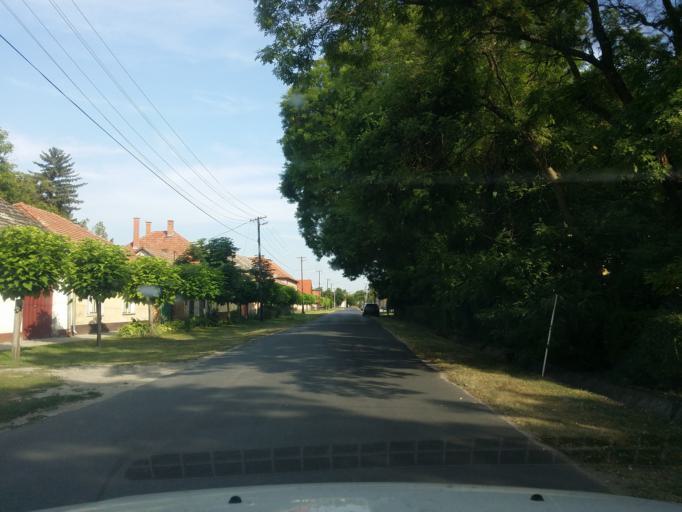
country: HU
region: Bacs-Kiskun
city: Jaszszentlaszlo
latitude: 46.5684
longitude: 19.7604
